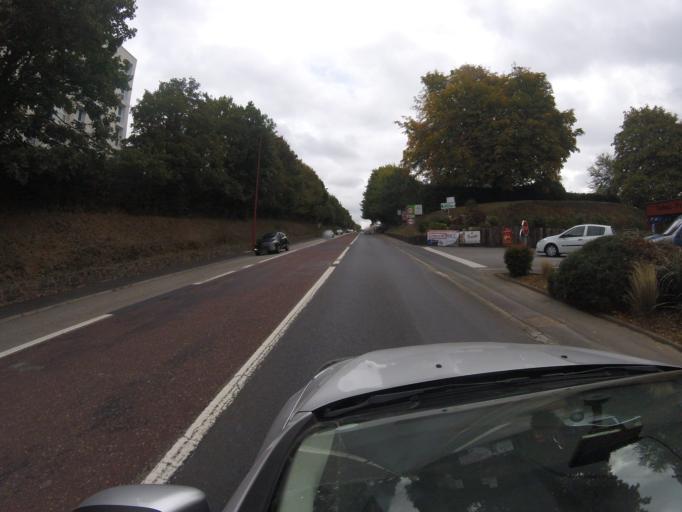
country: FR
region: Lower Normandy
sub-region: Departement de la Manche
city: Cherbourg-Octeville
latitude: 49.6187
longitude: -1.6109
